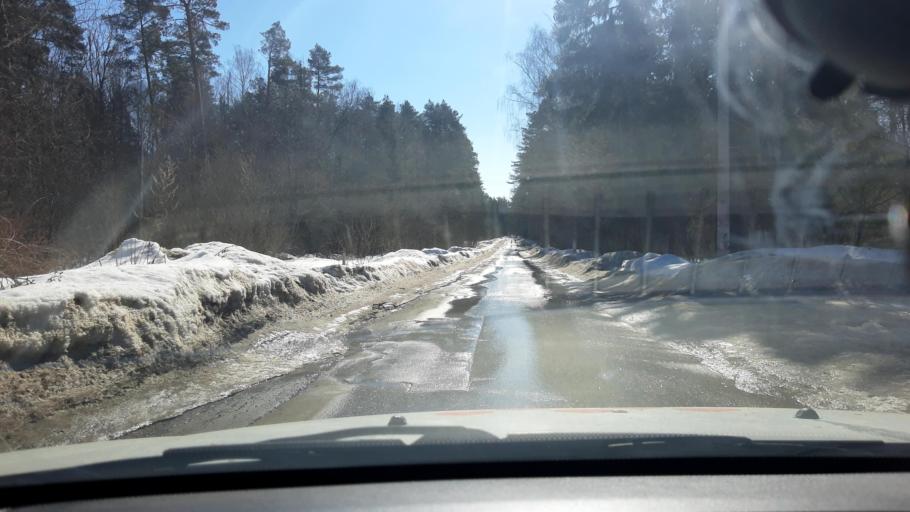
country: RU
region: Nizjnij Novgorod
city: Afonino
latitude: 56.1690
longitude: 44.0889
